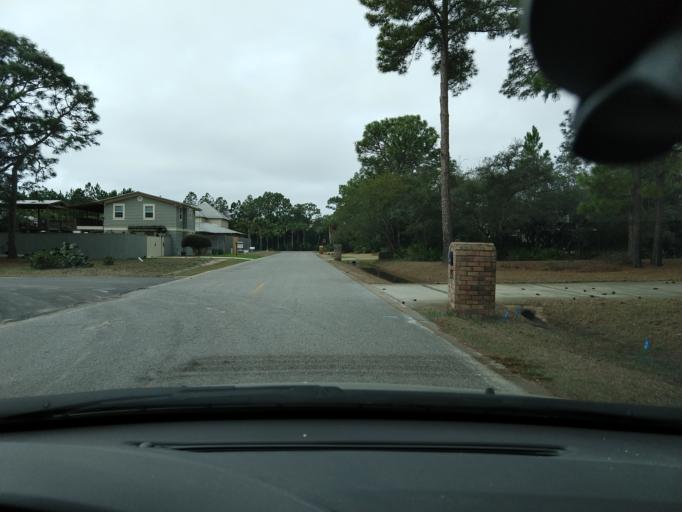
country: US
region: Florida
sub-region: Walton County
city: Miramar Beach
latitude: 30.4088
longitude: -86.3113
